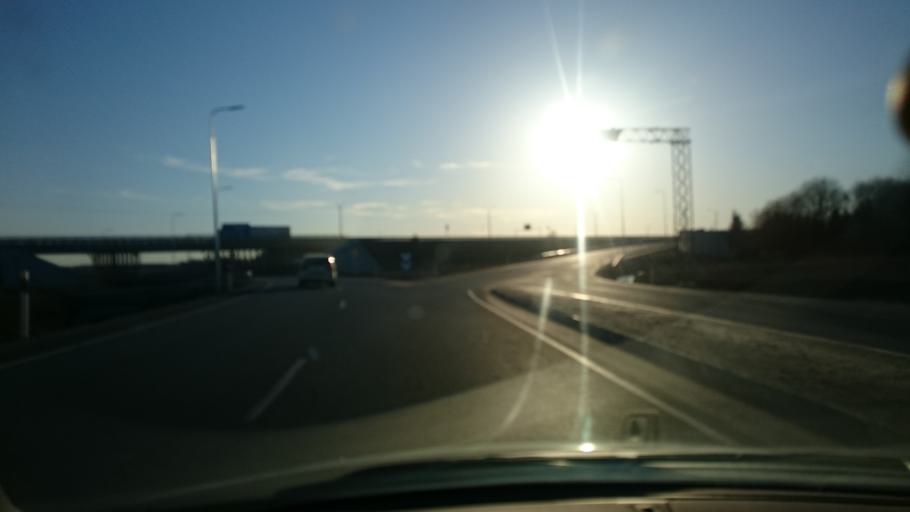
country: EE
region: Harju
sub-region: Rae vald
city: Jueri
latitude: 59.3550
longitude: 24.8826
